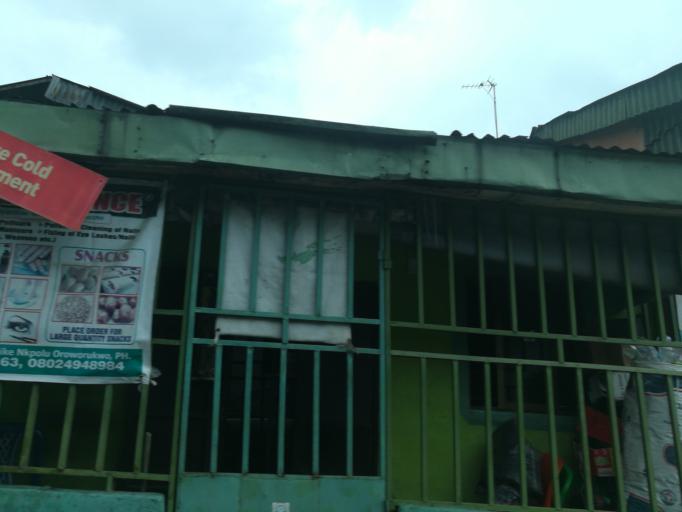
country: NG
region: Rivers
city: Port Harcourt
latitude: 4.8074
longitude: 6.9896
